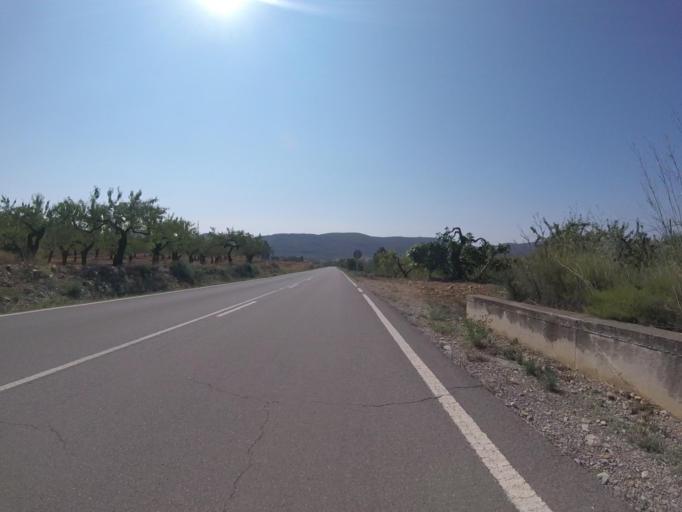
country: ES
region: Valencia
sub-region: Provincia de Castello
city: Adzaneta
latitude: 40.2298
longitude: -0.1759
